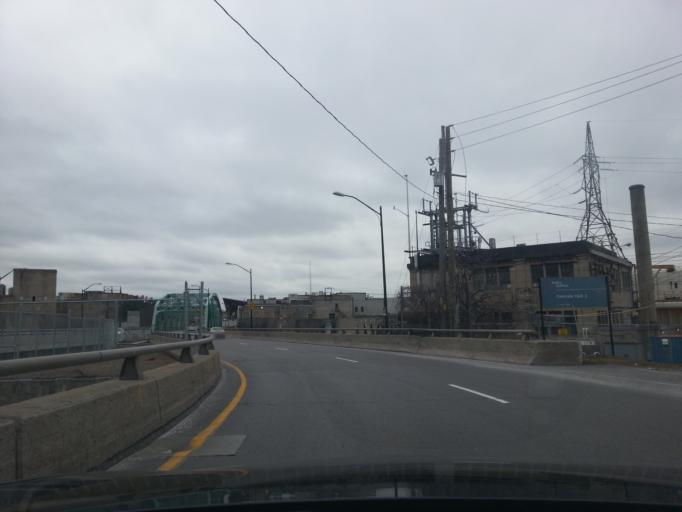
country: CA
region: Ontario
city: Ottawa
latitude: 45.4227
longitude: -75.7196
